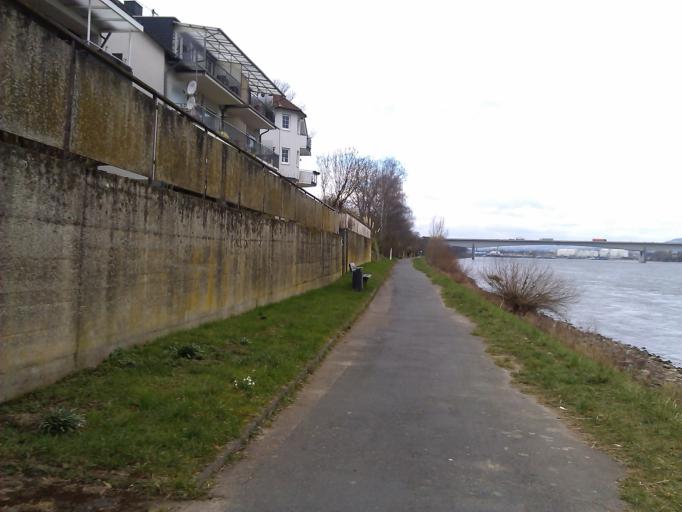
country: DE
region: Rheinland-Pfalz
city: Sankt Sebastian
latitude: 50.4021
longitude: 7.5795
